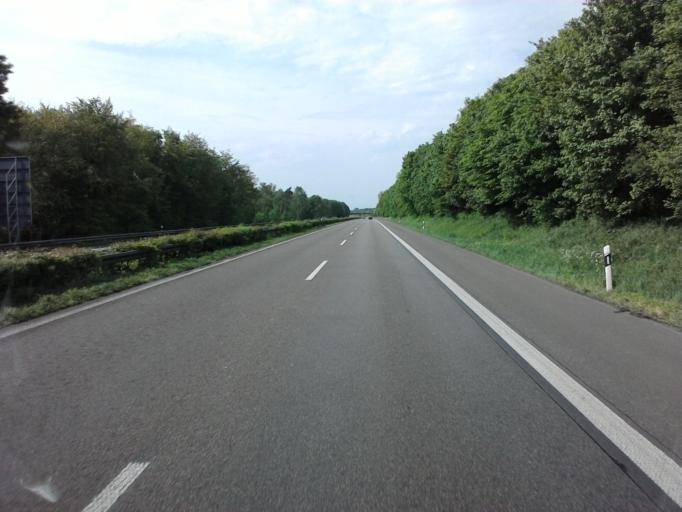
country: DE
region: North Rhine-Westphalia
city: Rheinberg
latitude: 51.5358
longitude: 6.5744
